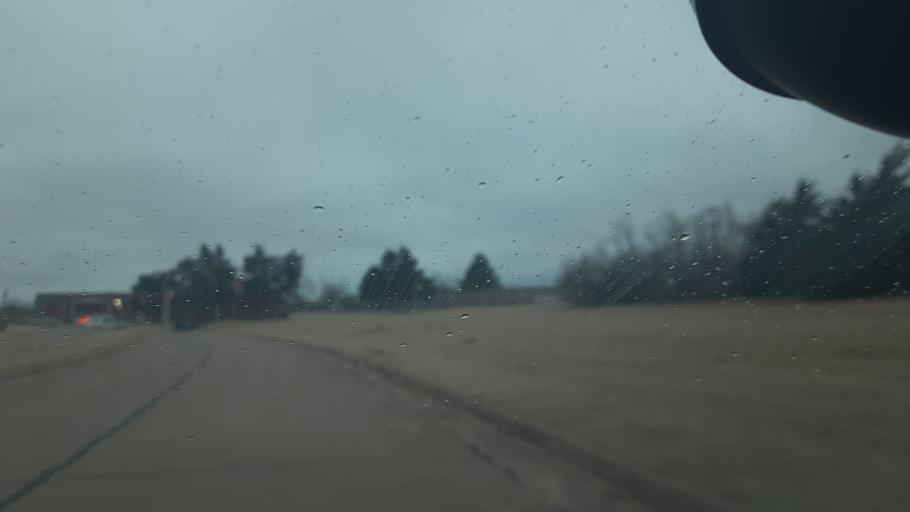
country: US
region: Oklahoma
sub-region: Logan County
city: Guthrie
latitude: 35.8755
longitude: -97.4005
